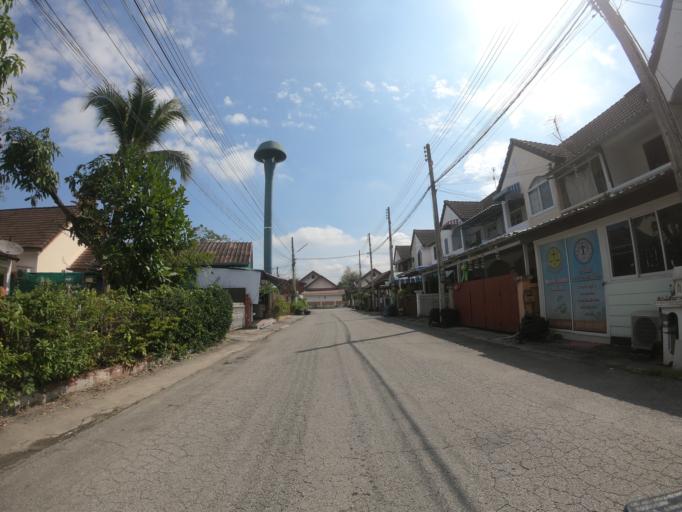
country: TH
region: Chiang Mai
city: Chiang Mai
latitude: 18.7351
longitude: 98.9598
